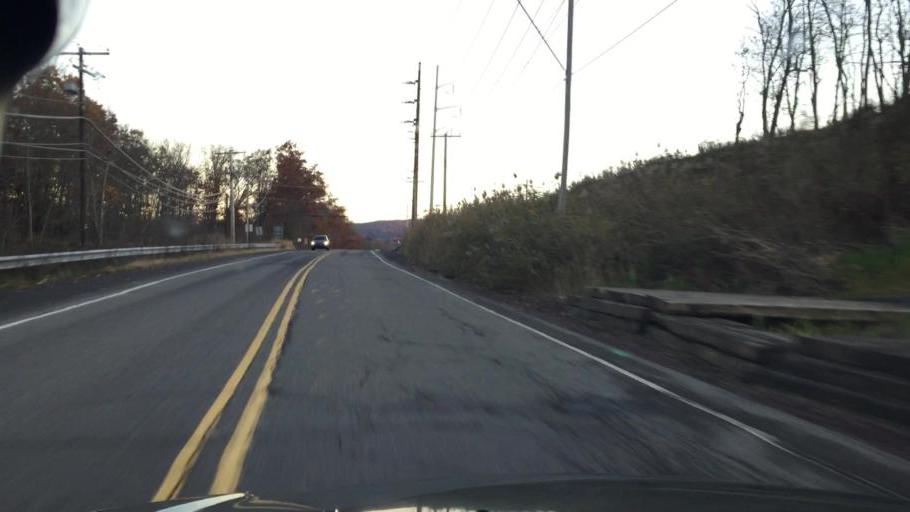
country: US
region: Pennsylvania
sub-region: Luzerne County
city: Mountain Top
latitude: 41.1409
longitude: -75.8967
